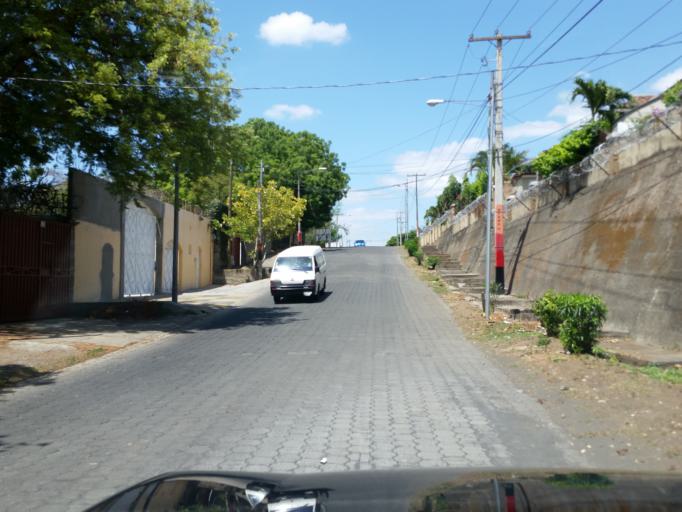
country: NI
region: Managua
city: Managua
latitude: 12.1146
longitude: -86.2764
